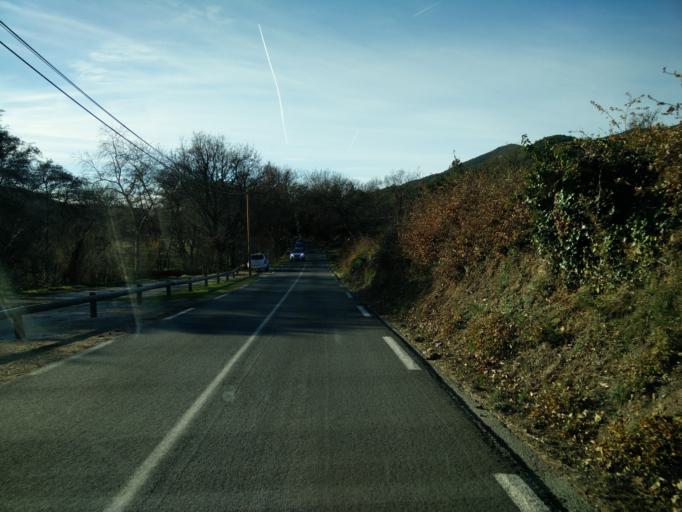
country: FR
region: Provence-Alpes-Cote d'Azur
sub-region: Departement du Var
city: Collobrieres
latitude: 43.2380
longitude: 6.2936
